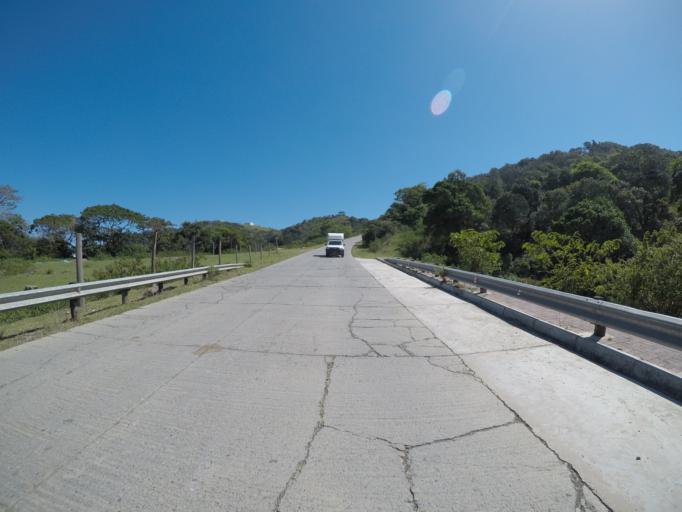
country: ZA
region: Eastern Cape
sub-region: OR Tambo District Municipality
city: Libode
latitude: -31.9768
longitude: 29.1481
